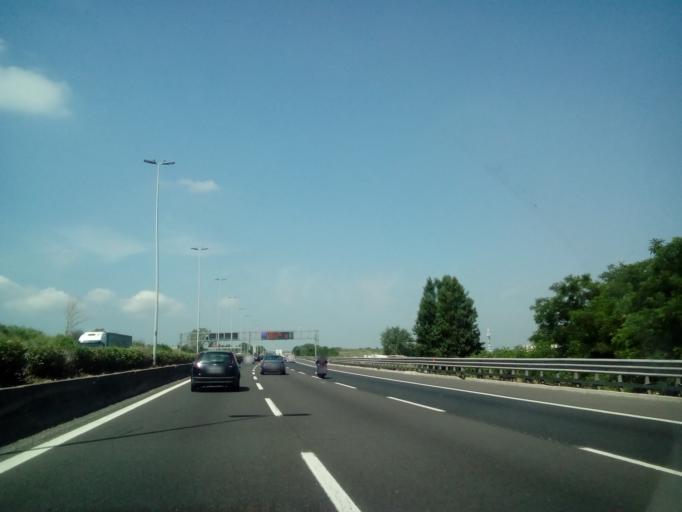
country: IT
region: Latium
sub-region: Citta metropolitana di Roma Capitale
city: Borgo Lotti
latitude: 41.7953
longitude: 12.5254
